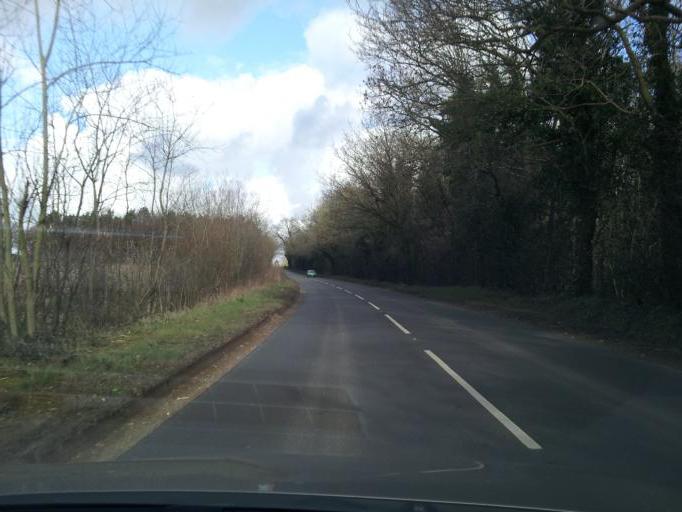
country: GB
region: England
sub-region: Norfolk
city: Mattishall
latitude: 52.6743
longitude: 1.1012
